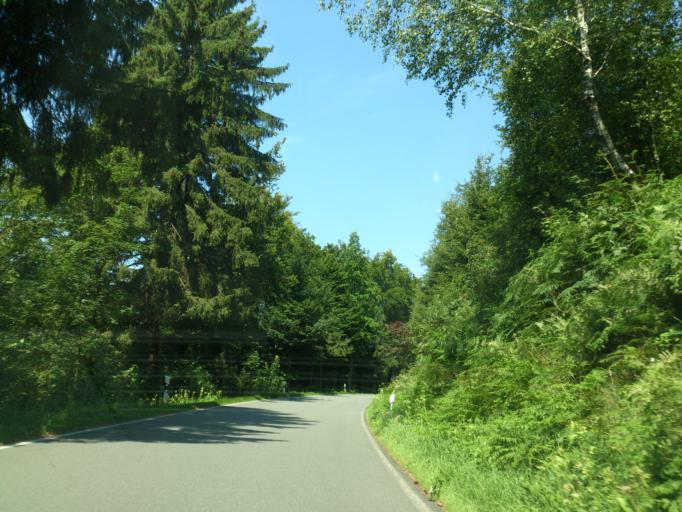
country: DE
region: North Rhine-Westphalia
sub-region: Regierungsbezirk Detmold
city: Altenbeken
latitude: 51.7792
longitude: 8.9571
